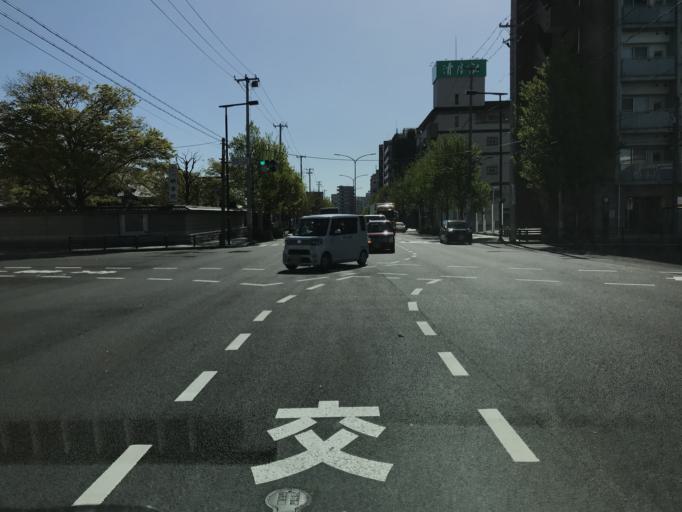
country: JP
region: Miyagi
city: Sendai-shi
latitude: 38.2557
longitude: 140.8907
